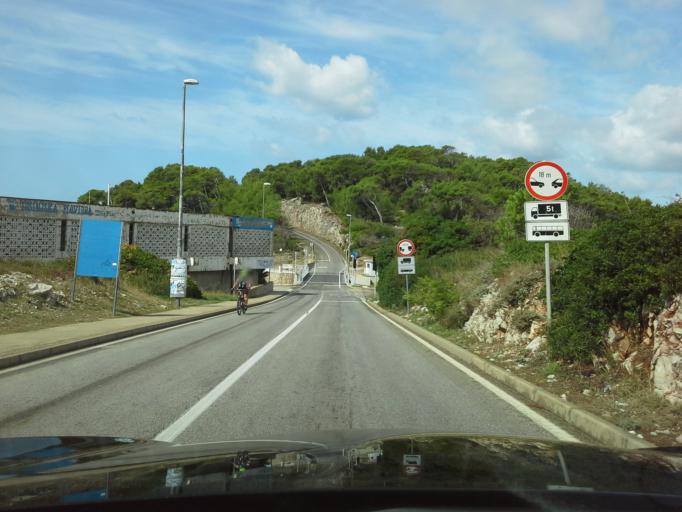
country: HR
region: Primorsko-Goranska
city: Mali Losinj
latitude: 44.5448
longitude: 14.4613
